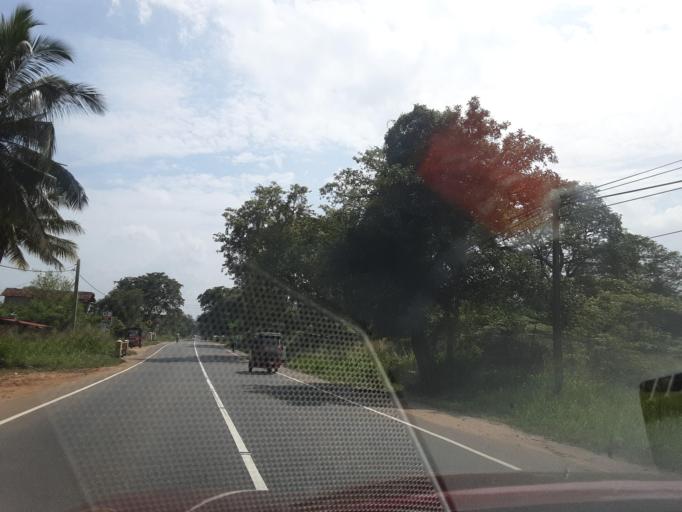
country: LK
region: Northern Province
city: Vavuniya
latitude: 8.5305
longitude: 80.4981
